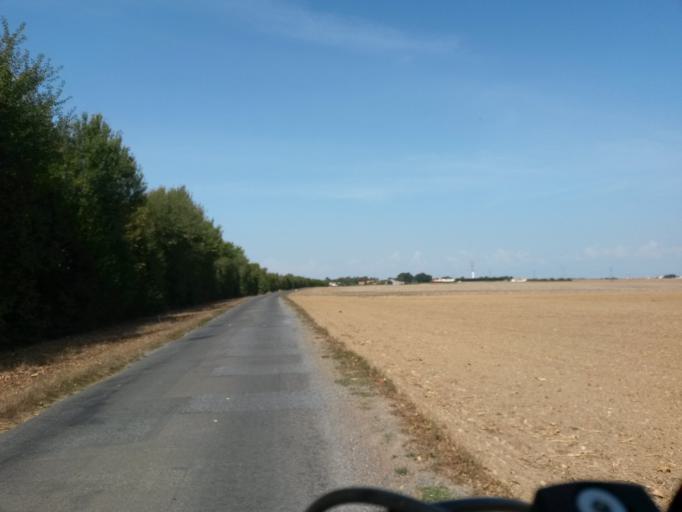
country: FR
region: Poitou-Charentes
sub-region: Departement de la Charente-Maritime
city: Puilboreau
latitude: 46.1919
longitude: -1.1304
